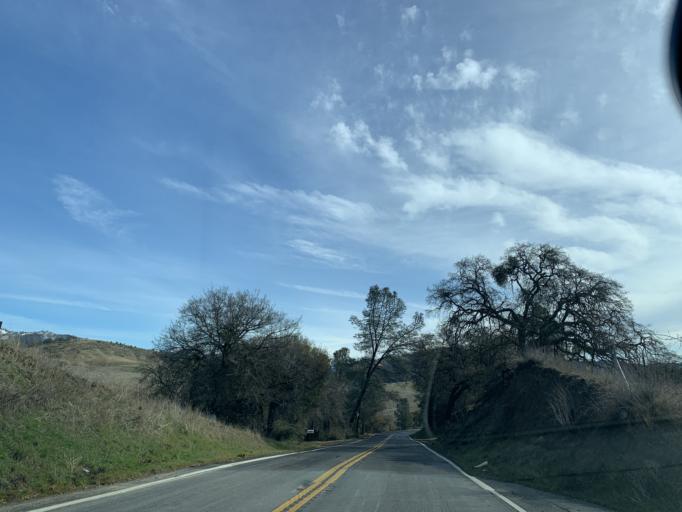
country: US
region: California
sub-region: Monterey County
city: Greenfield
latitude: 36.5079
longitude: -121.0965
